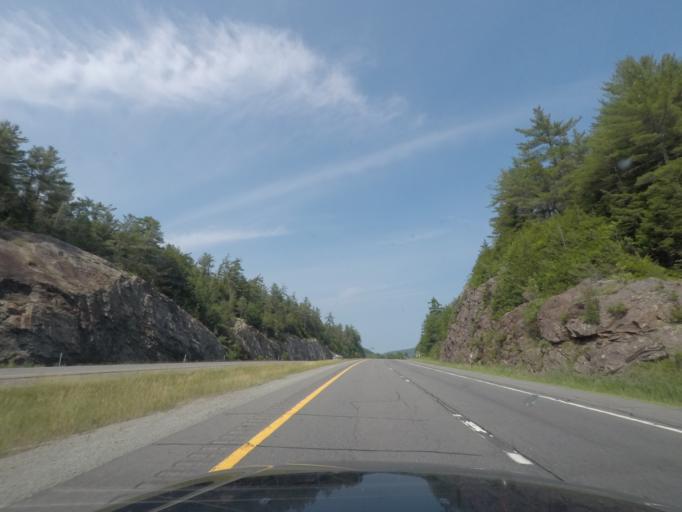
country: US
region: New York
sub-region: Essex County
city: Mineville
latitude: 44.1105
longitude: -73.6109
